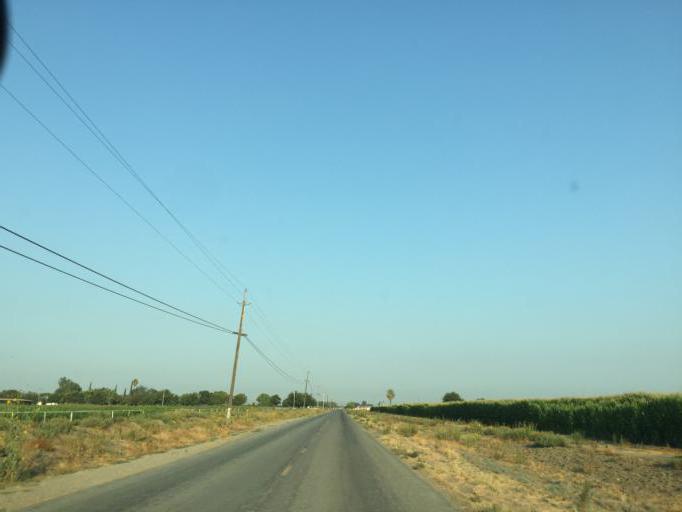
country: US
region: California
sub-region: Tulare County
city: London
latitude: 36.4436
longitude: -119.3593
